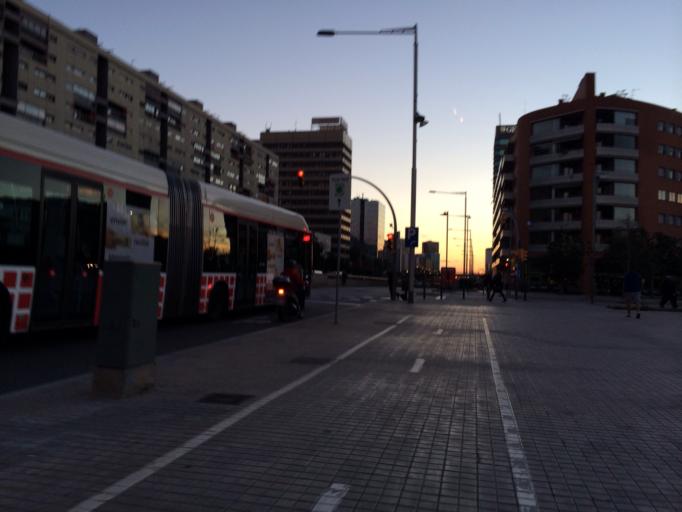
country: ES
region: Catalonia
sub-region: Provincia de Barcelona
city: Sants-Montjuic
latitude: 41.3668
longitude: 2.1378
